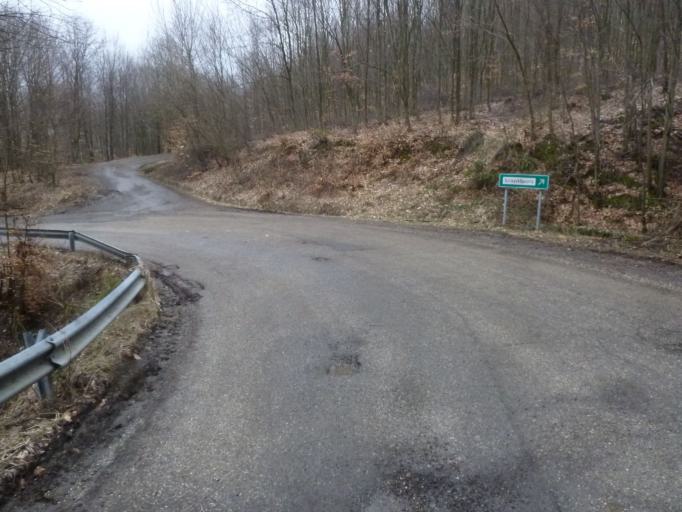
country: HU
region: Nograd
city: Kazar
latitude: 48.1240
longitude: 19.9003
